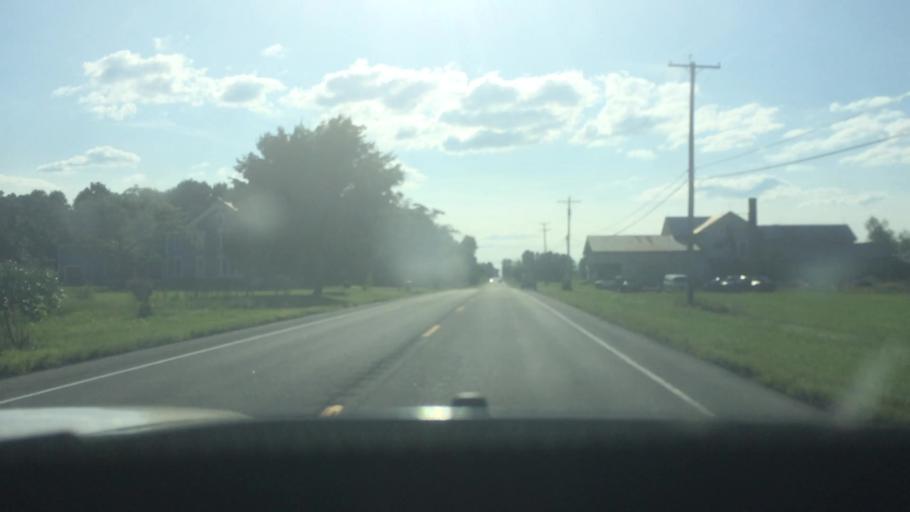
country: US
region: New York
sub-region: St. Lawrence County
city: Hannawa Falls
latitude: 44.6924
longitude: -74.6769
